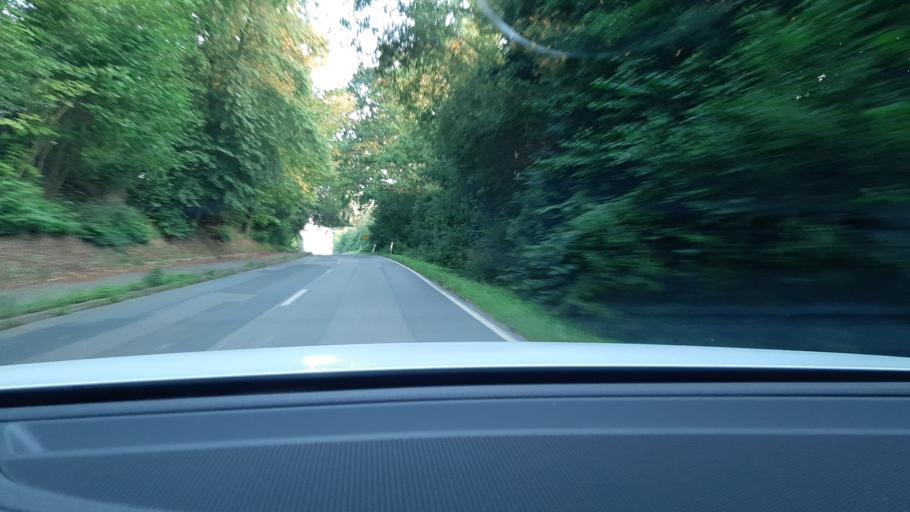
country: DE
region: Schleswig-Holstein
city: Klein Wesenberg
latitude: 53.8159
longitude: 10.5420
